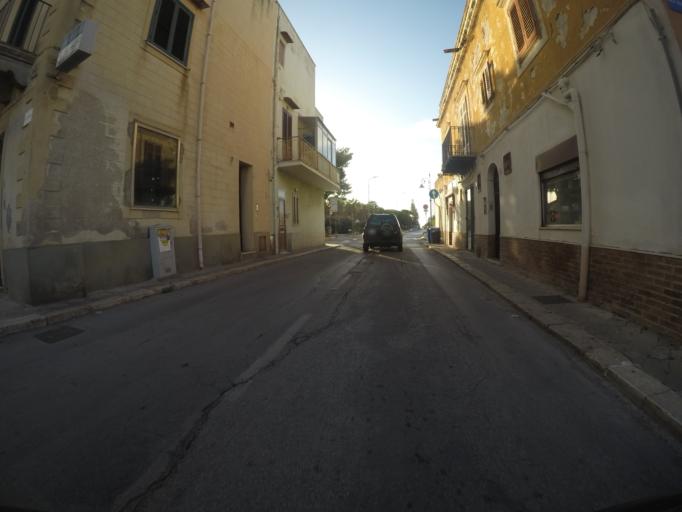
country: IT
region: Sicily
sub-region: Palermo
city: Isola delle Femmine
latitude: 38.1985
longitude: 13.2481
